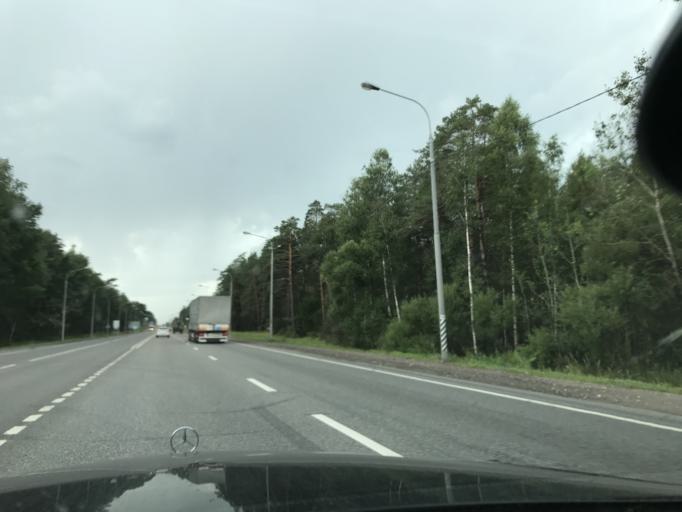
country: RU
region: Vladimir
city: Pokrov
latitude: 55.9218
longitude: 39.2256
